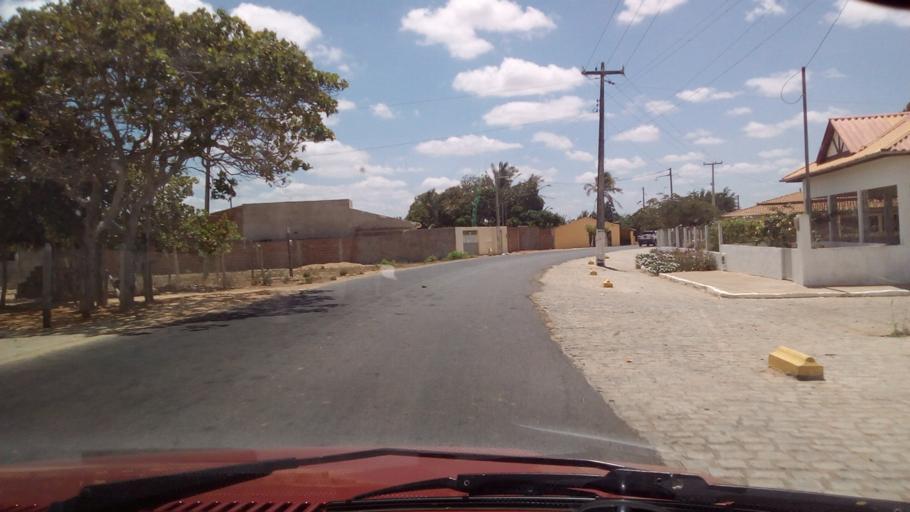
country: BR
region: Paraiba
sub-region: Cacimba De Dentro
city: Cacimba de Dentro
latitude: -6.6255
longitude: -35.7984
